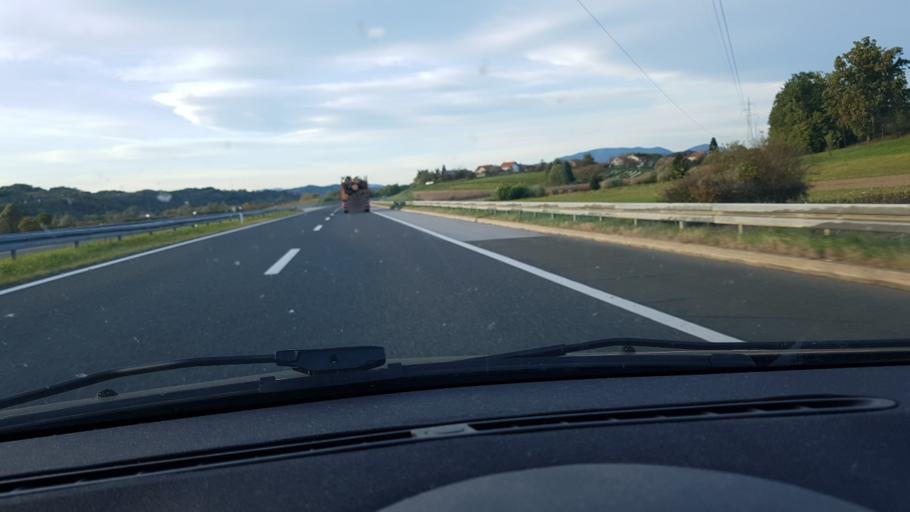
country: HR
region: Krapinsko-Zagorska
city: Zabok
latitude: 46.0504
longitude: 15.9218
